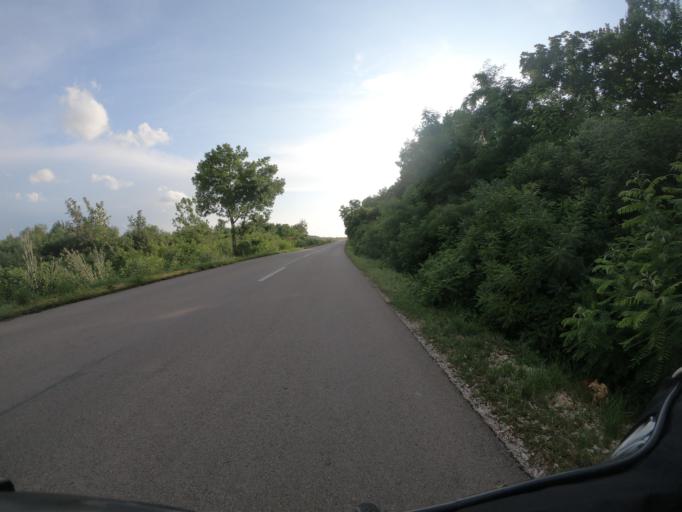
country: HU
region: Borsod-Abauj-Zemplen
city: Mezokeresztes
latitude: 47.8200
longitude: 20.7507
